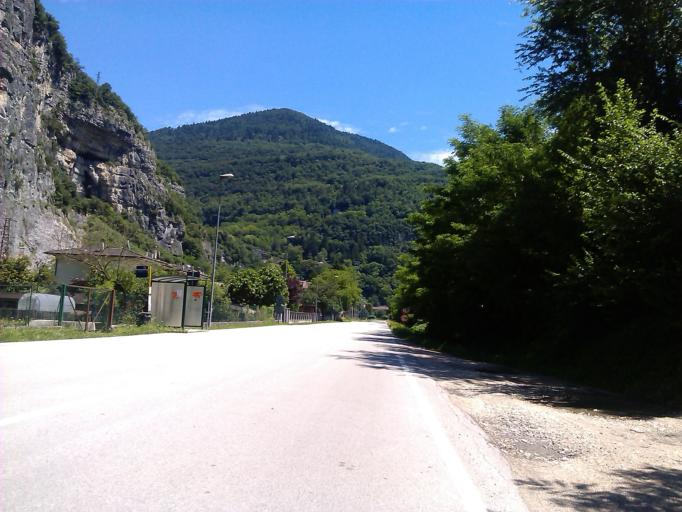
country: IT
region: Veneto
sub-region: Provincia di Vicenza
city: Enego
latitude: 45.9655
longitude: 11.7021
